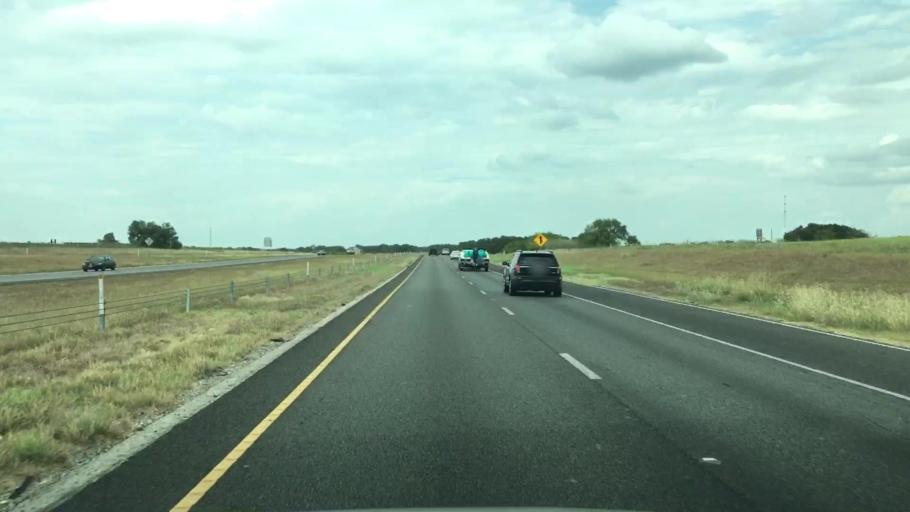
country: US
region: Texas
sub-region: Bexar County
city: Elmendorf
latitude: 29.1418
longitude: -98.4287
